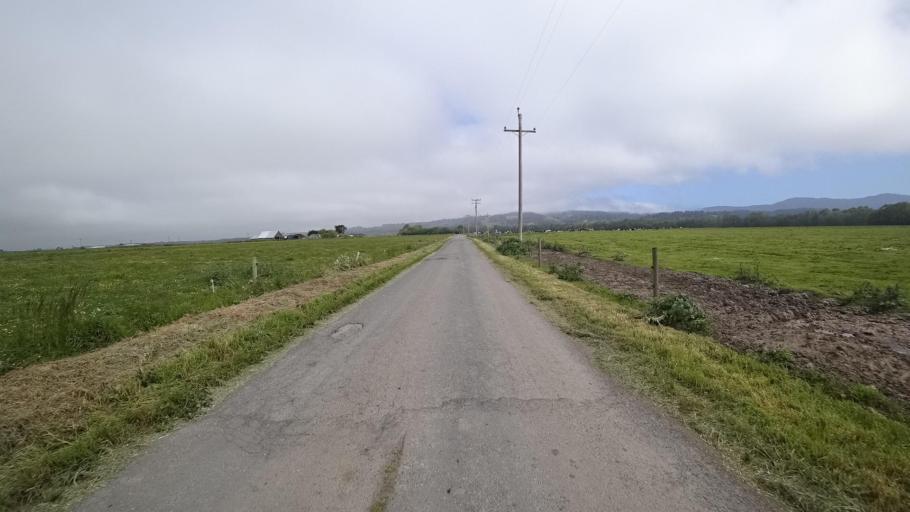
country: US
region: California
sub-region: Humboldt County
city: Fortuna
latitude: 40.5855
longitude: -124.1879
